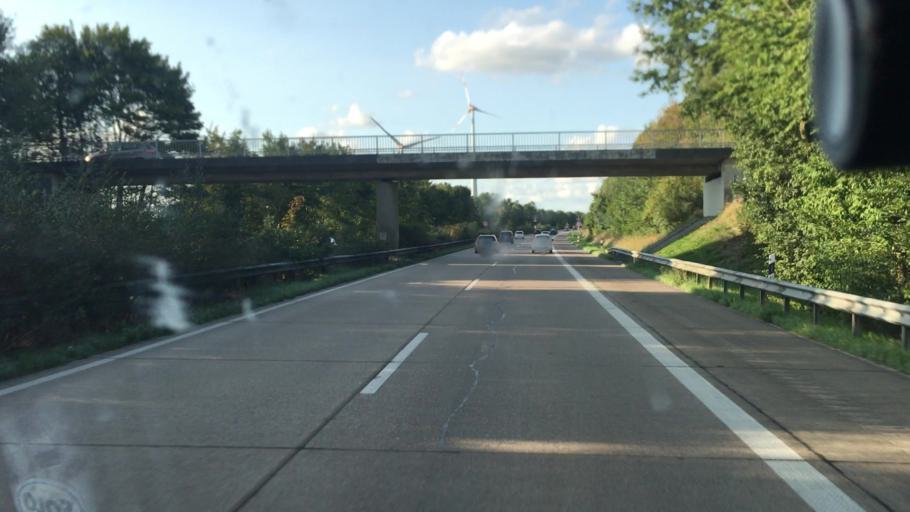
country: DE
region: Lower Saxony
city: Sande
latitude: 53.4968
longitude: 7.9977
